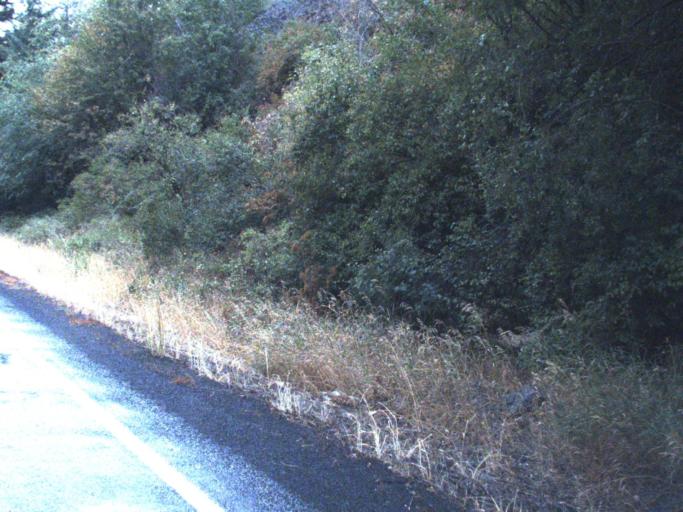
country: US
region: Washington
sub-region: Spokane County
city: Medical Lake
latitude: 47.7579
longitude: -117.8909
